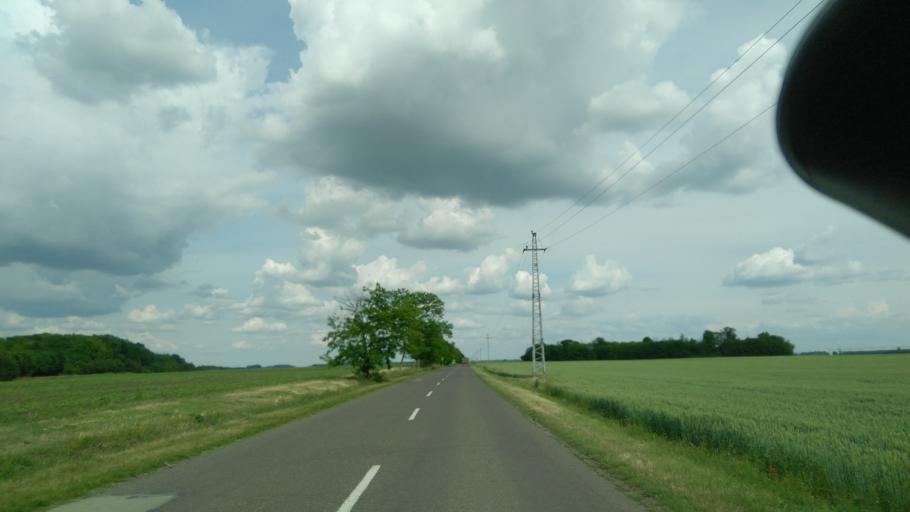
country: HU
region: Bekes
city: Mezohegyes
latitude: 46.3148
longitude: 20.8369
